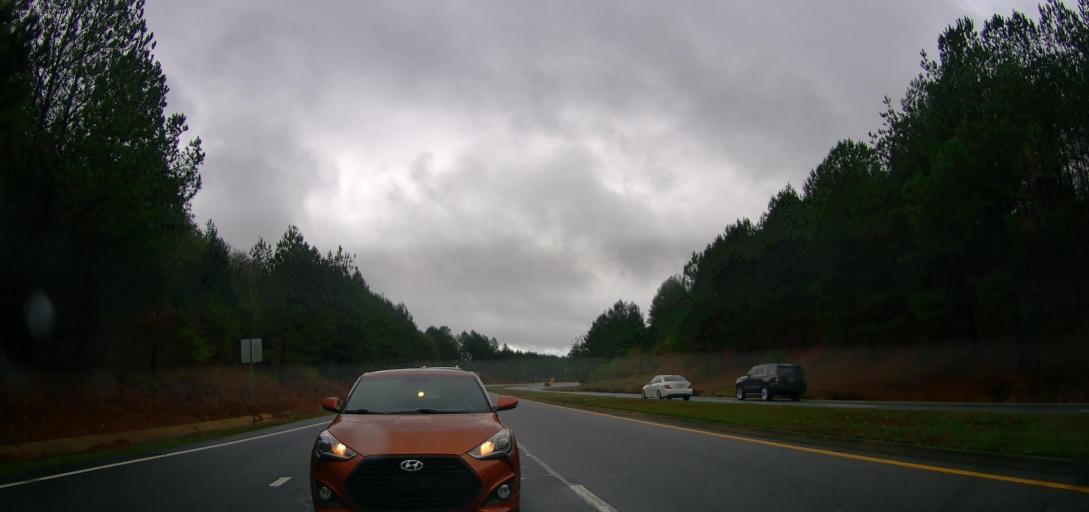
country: US
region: Georgia
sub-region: Oconee County
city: Watkinsville
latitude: 33.9076
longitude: -83.4041
